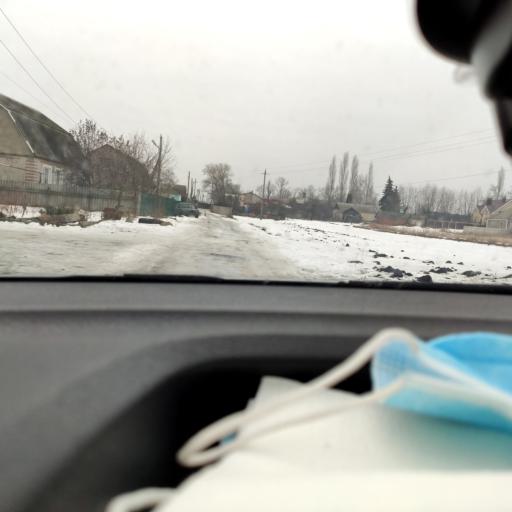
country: RU
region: Voronezj
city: Novaya Usman'
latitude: 51.6368
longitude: 39.3905
